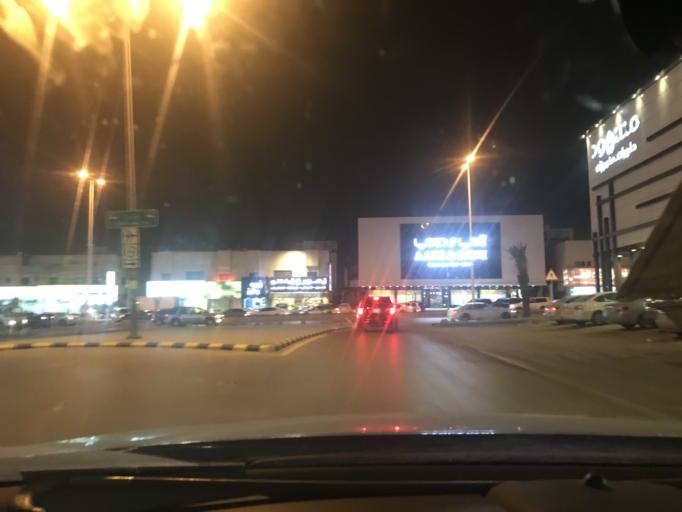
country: SA
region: Ar Riyad
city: Riyadh
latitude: 24.7439
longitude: 46.7541
